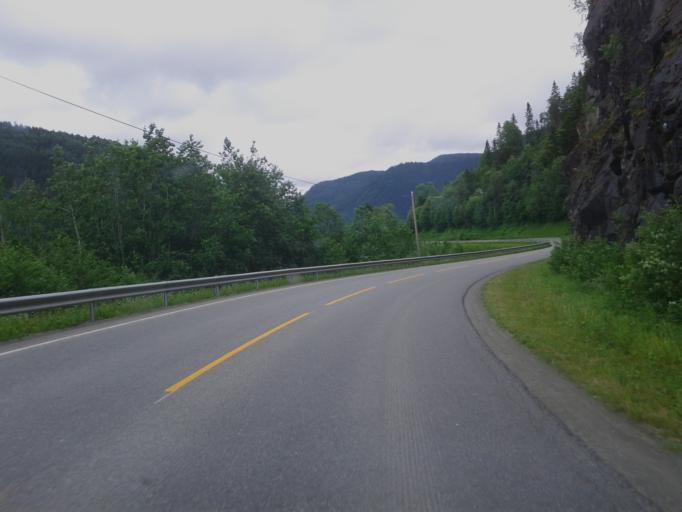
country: NO
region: Sor-Trondelag
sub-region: Midtre Gauldal
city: Storen
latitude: 63.0206
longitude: 10.3235
